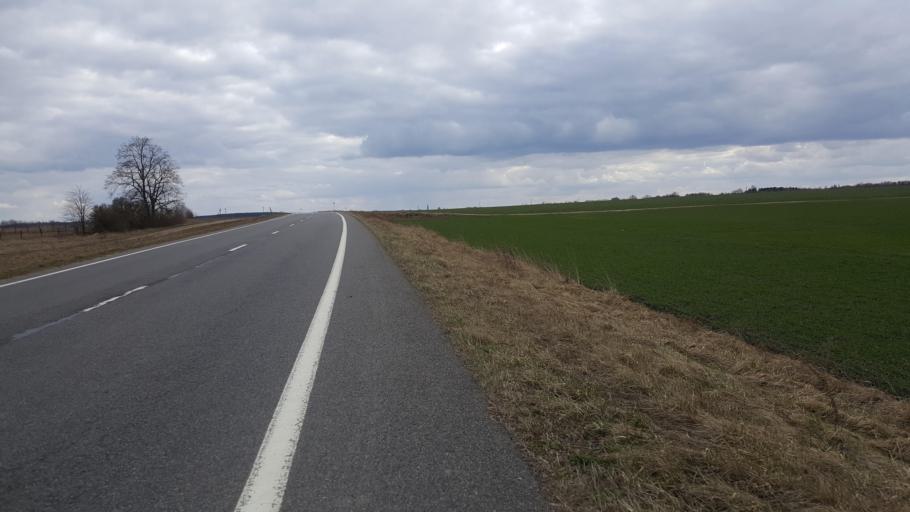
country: BY
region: Brest
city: Kamyanyets
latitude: 52.4381
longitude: 23.8291
